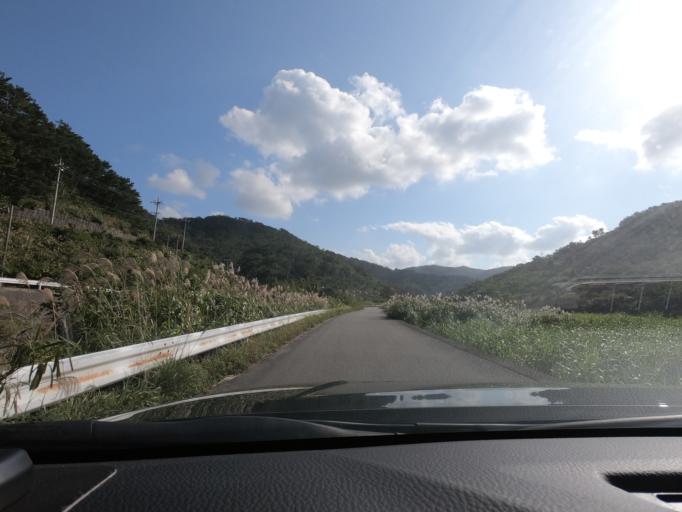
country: JP
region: Okinawa
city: Nago
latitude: 26.7664
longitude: 128.2079
